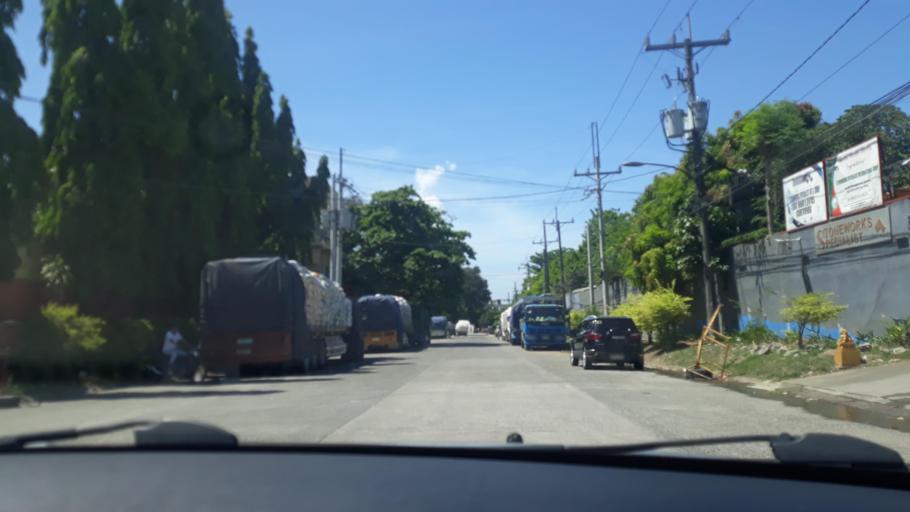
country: PH
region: Calabarzon
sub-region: Province of Cavite
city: Manggahan
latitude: 14.2957
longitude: 120.9176
